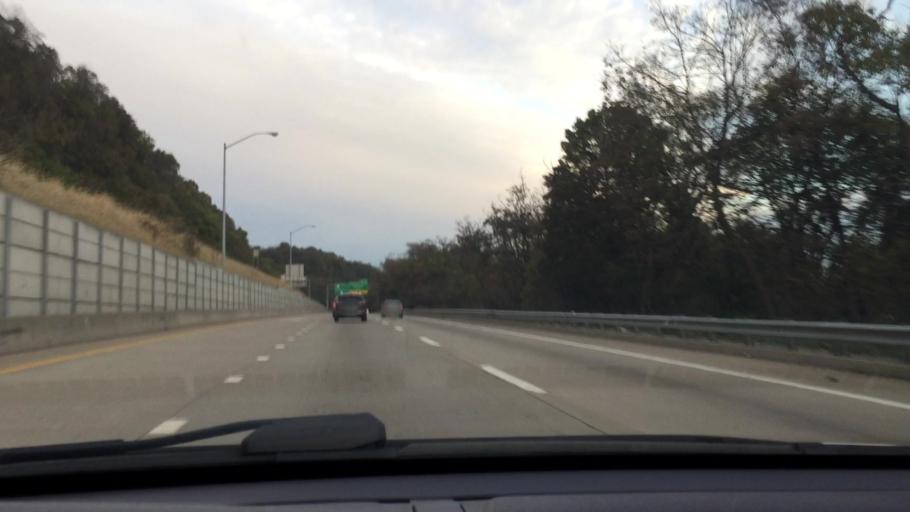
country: US
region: Pennsylvania
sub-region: Allegheny County
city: Sharpsburg
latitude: 40.4970
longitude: -79.9342
